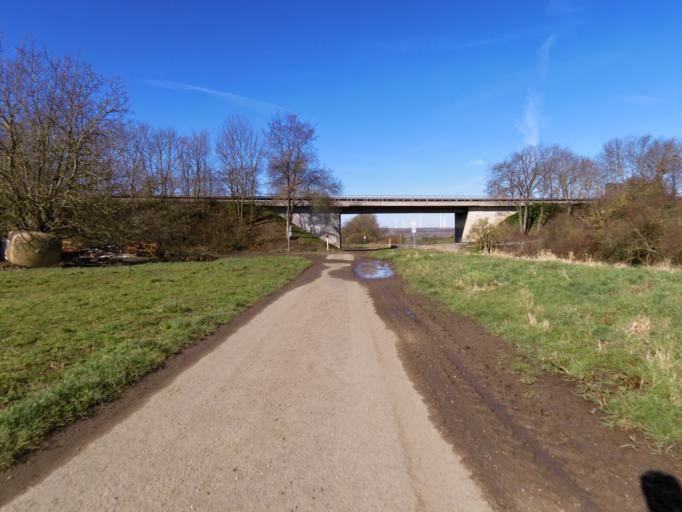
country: DE
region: Rheinland-Pfalz
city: Offstein
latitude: 49.6080
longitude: 8.2287
